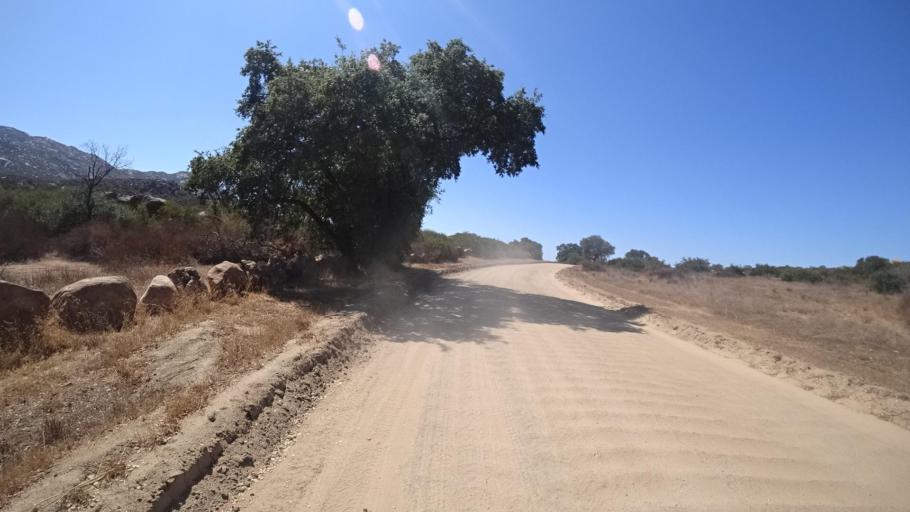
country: US
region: California
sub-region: San Diego County
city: San Diego Country Estates
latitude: 32.9489
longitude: -116.8286
